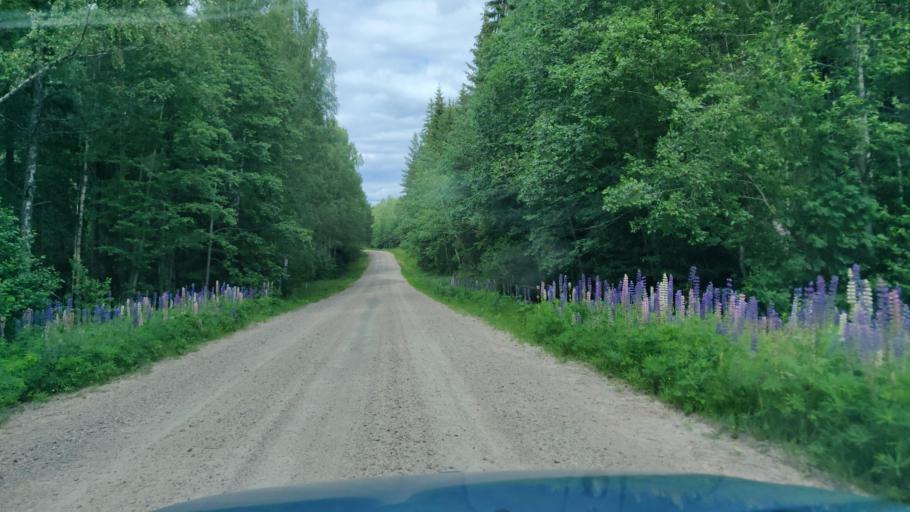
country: SE
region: Vaermland
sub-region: Hagfors Kommun
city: Hagfors
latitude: 60.0359
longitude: 13.7196
